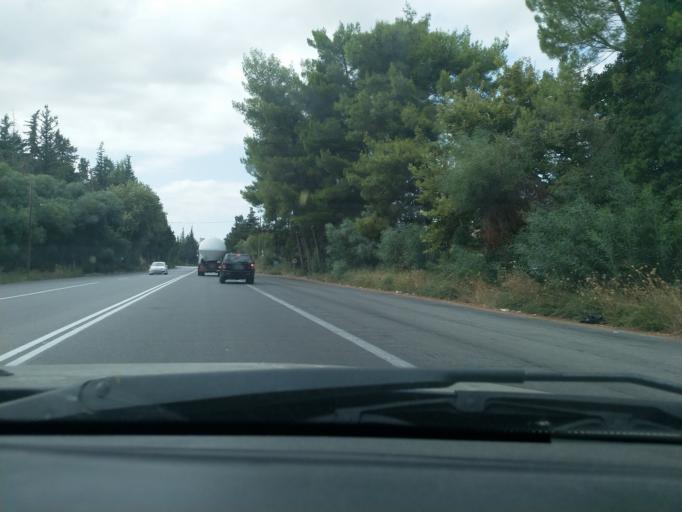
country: GR
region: Crete
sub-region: Nomos Chanias
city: Georgioupolis
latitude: 35.3656
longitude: 24.2189
